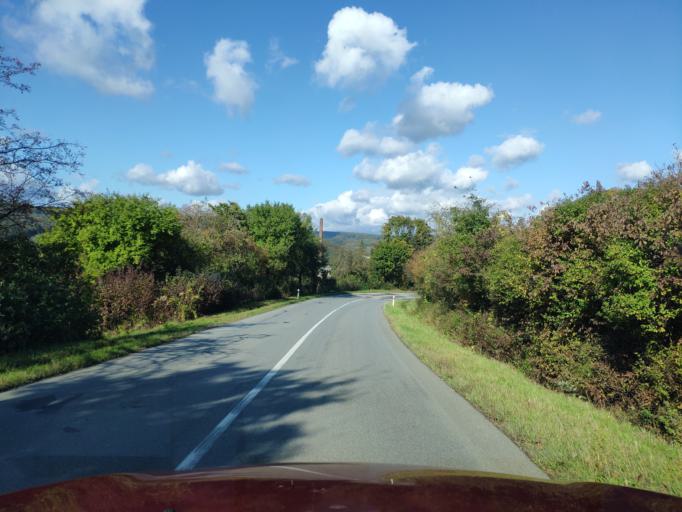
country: SK
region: Presovsky
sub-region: Okres Presov
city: Presov
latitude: 48.8883
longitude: 21.2620
